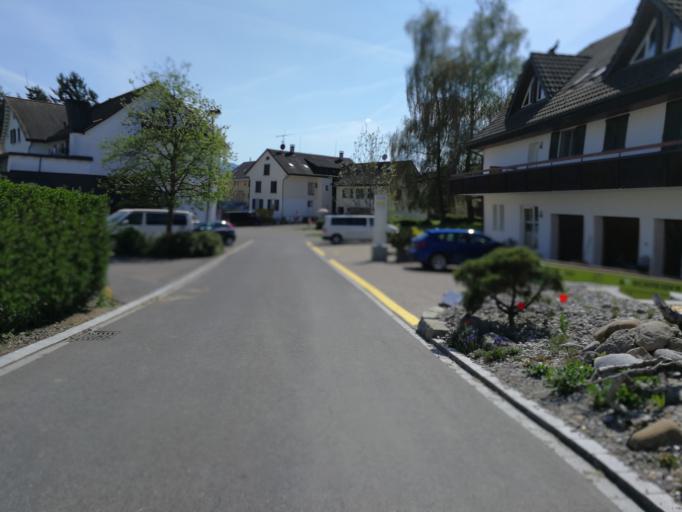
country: CH
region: Zurich
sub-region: Bezirk Meilen
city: Hombrechtikon
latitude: 47.2516
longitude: 8.7637
